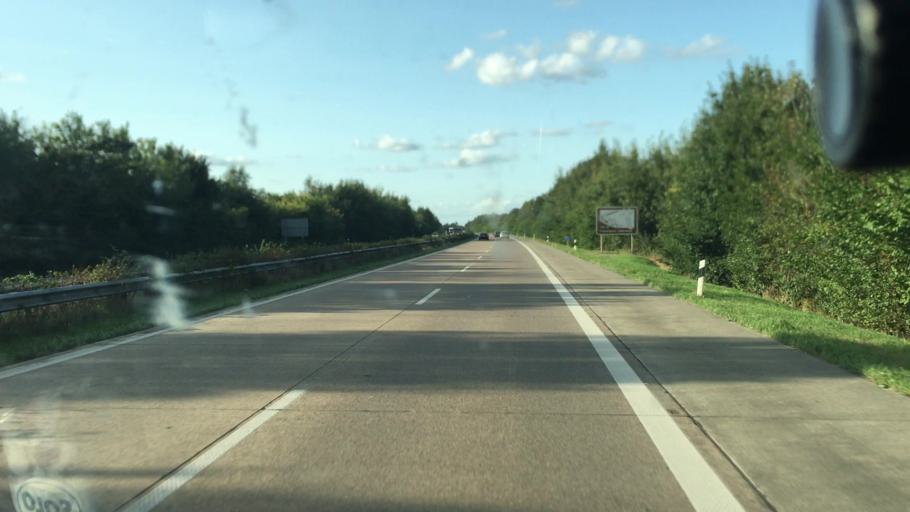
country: DE
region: Lower Saxony
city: Wiefelstede
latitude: 53.3072
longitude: 8.1446
